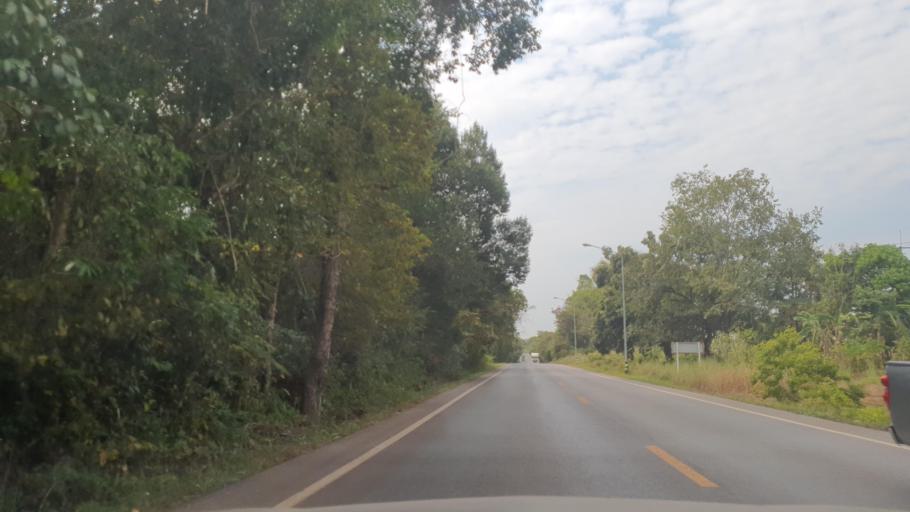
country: TH
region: Changwat Bueng Kan
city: Bung Khla
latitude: 18.2902
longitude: 103.9097
